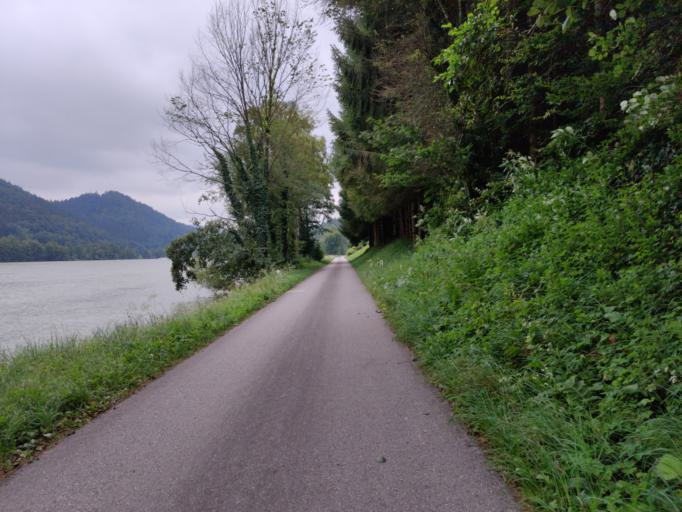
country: AT
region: Lower Austria
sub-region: Politischer Bezirk Melk
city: Nochling
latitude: 48.2223
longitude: 14.9456
